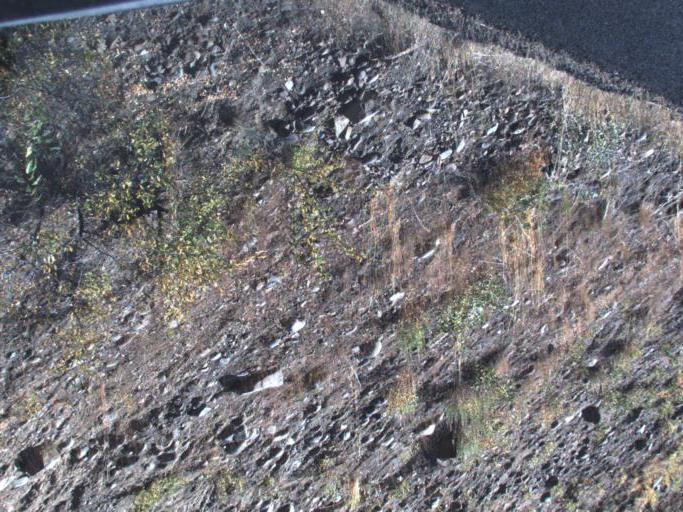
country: US
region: Washington
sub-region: Yakima County
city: Tieton
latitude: 46.7011
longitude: -120.8996
